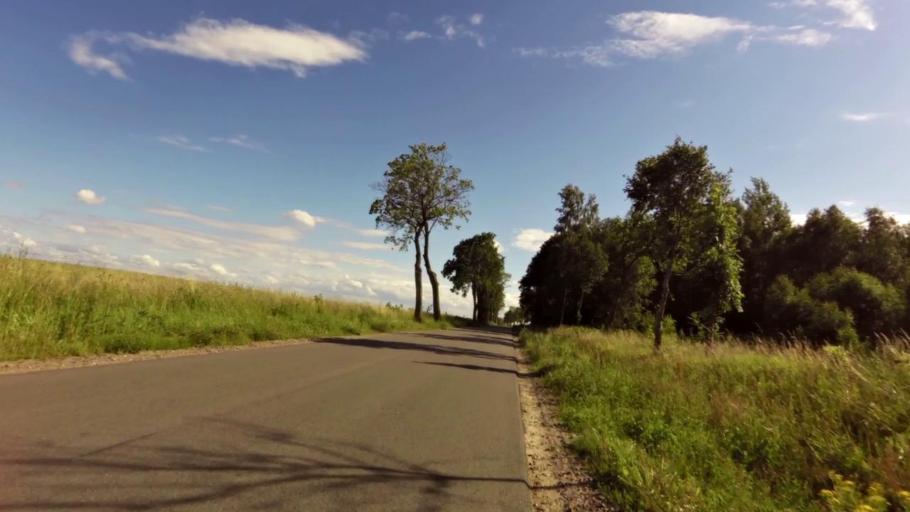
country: PL
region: West Pomeranian Voivodeship
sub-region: Powiat slawienski
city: Slawno
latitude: 54.4515
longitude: 16.7382
